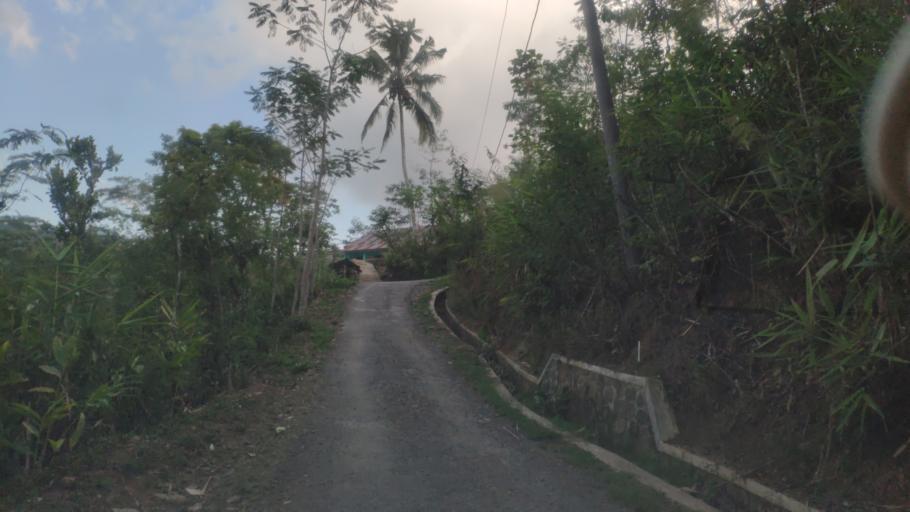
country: ID
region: Central Java
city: Buaran
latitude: -7.2479
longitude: 109.5736
